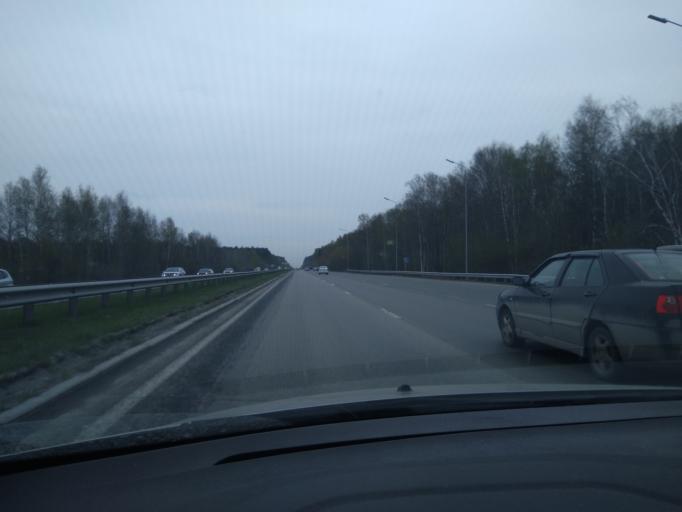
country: RU
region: Sverdlovsk
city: Istok
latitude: 56.8210
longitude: 60.7152
